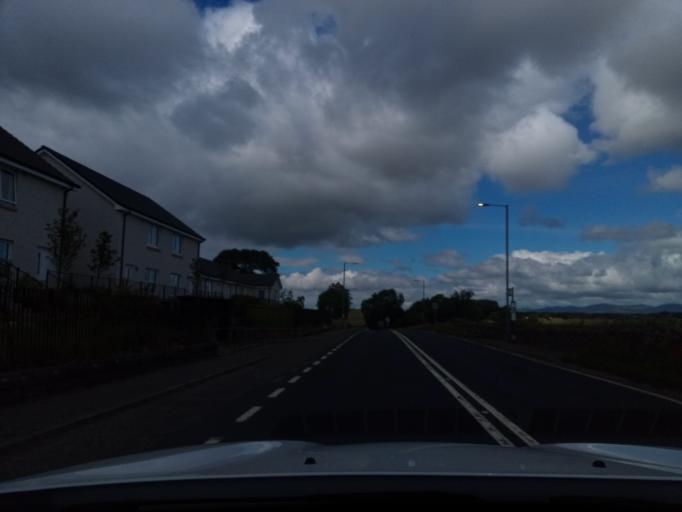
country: GB
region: Scotland
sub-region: Fife
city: Cairneyhill
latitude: 56.0502
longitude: -3.5311
